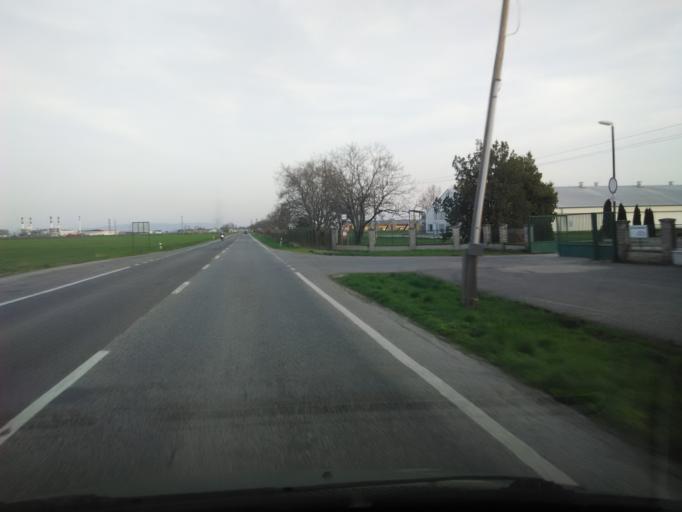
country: SK
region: Nitriansky
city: Levice
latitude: 48.2002
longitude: 18.5867
